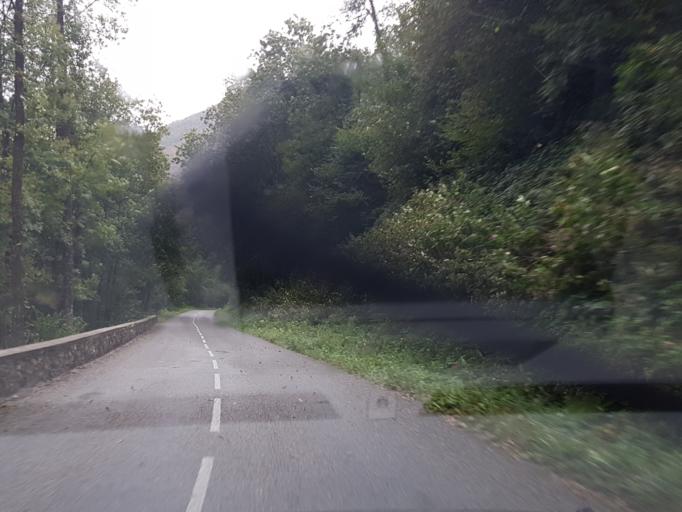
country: FR
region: Midi-Pyrenees
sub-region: Departement de l'Ariege
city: Saint-Girons
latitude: 42.9130
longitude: 1.2673
